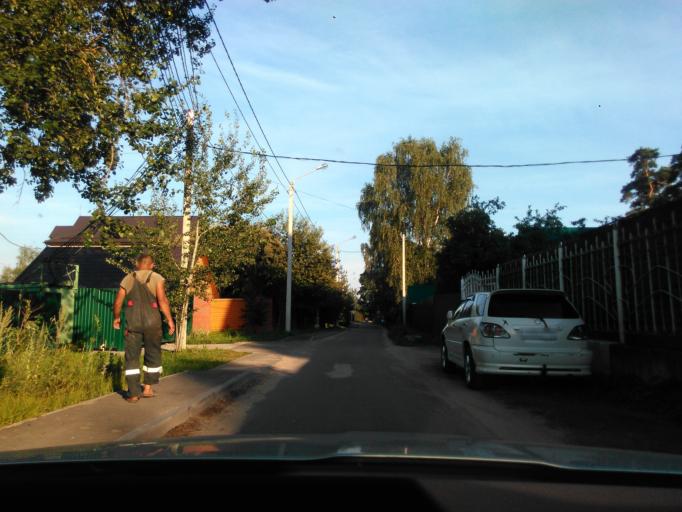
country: RU
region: Tverskaya
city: Konakovo
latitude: 56.7582
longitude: 36.7466
